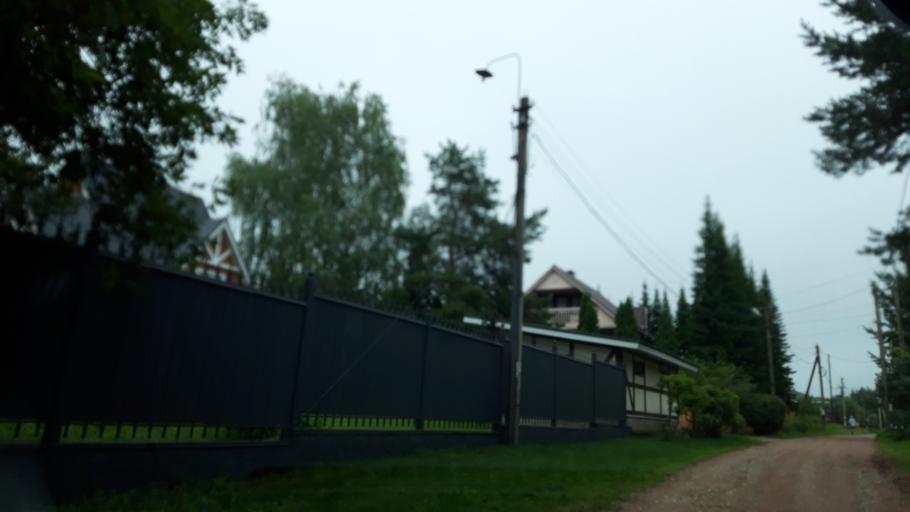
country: RU
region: Tverskaya
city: Konakovo
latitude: 56.6600
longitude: 36.6544
